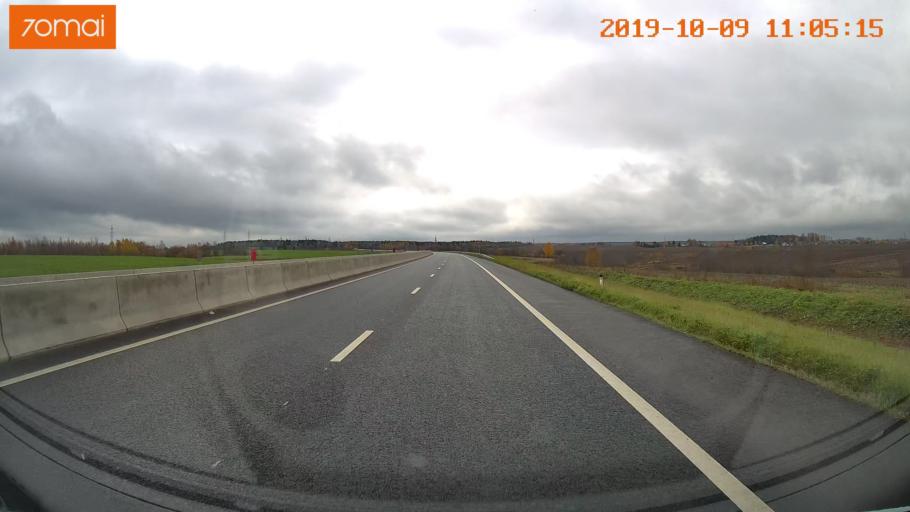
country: RU
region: Vologda
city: Molochnoye
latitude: 59.2024
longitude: 39.7600
